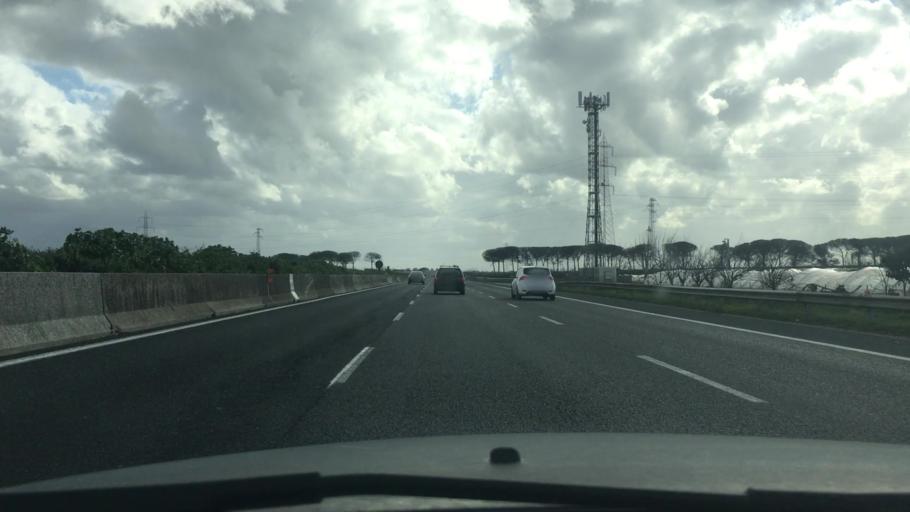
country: IT
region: Campania
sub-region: Provincia di Napoli
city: Pascarola
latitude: 40.9917
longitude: 14.3247
